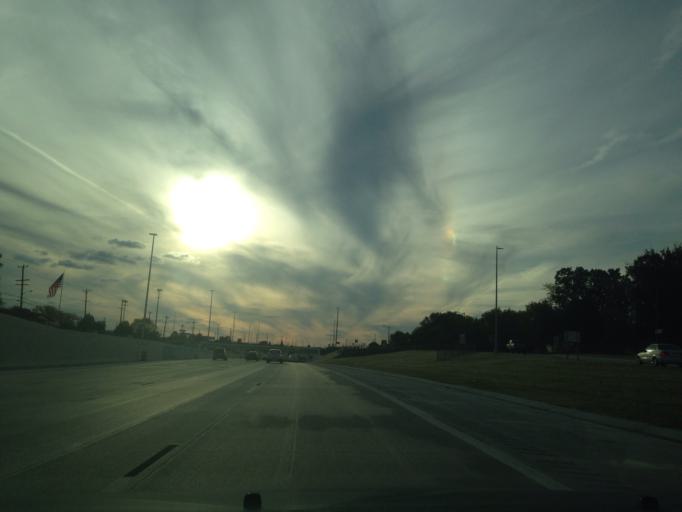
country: US
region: Michigan
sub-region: Wayne County
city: Redford
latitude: 42.3848
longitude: -83.3094
